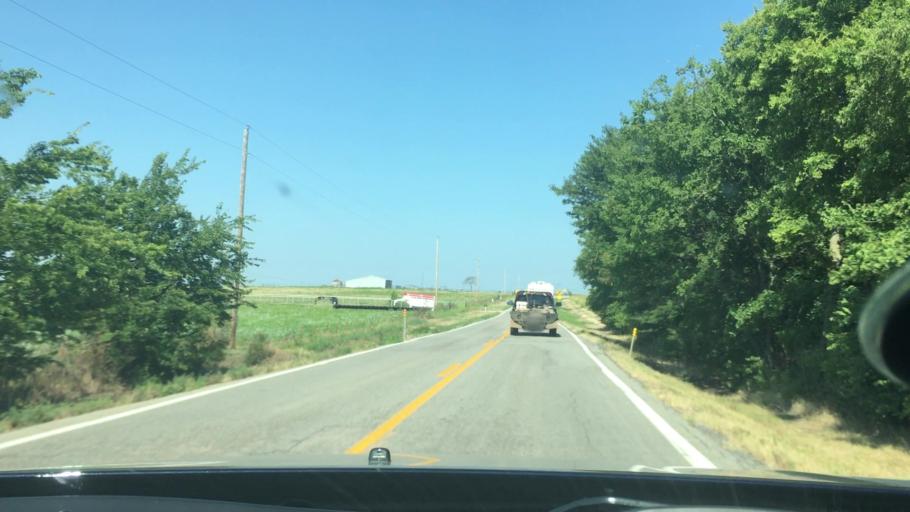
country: US
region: Oklahoma
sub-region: Johnston County
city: Tishomingo
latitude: 34.1869
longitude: -96.5225
